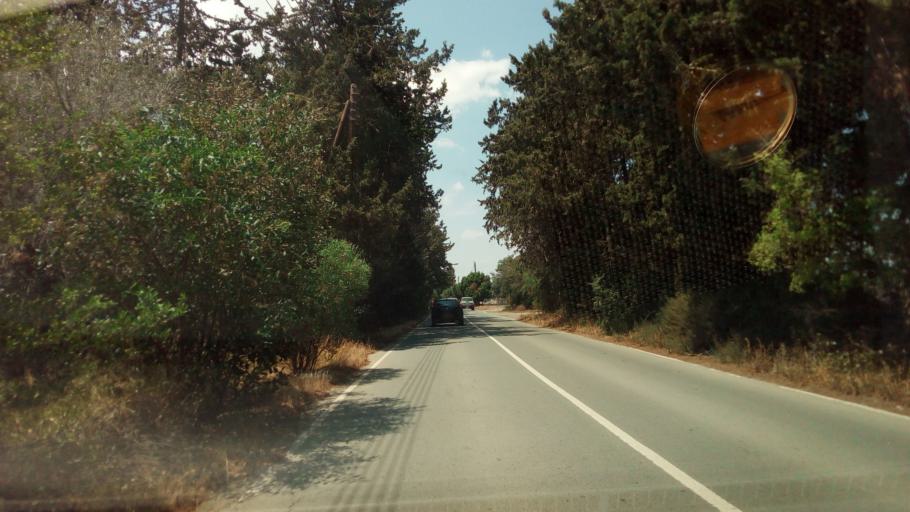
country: CY
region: Larnaka
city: Meneou
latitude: 34.8583
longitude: 33.5977
